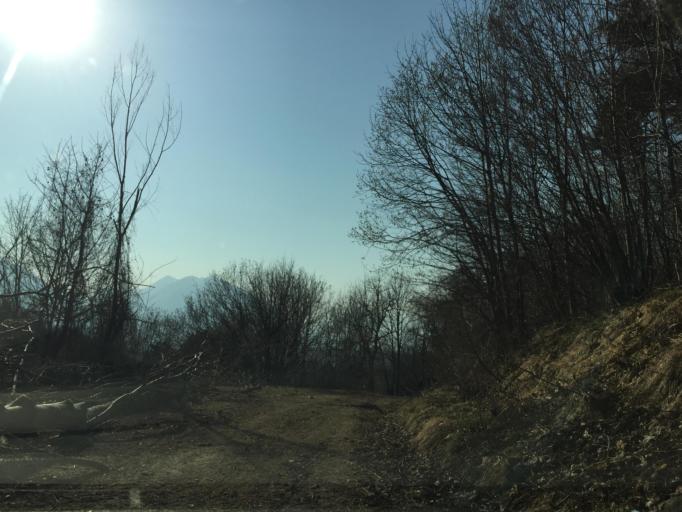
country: IT
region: Friuli Venezia Giulia
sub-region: Provincia di Udine
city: Amaro
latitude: 46.3867
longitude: 13.0711
